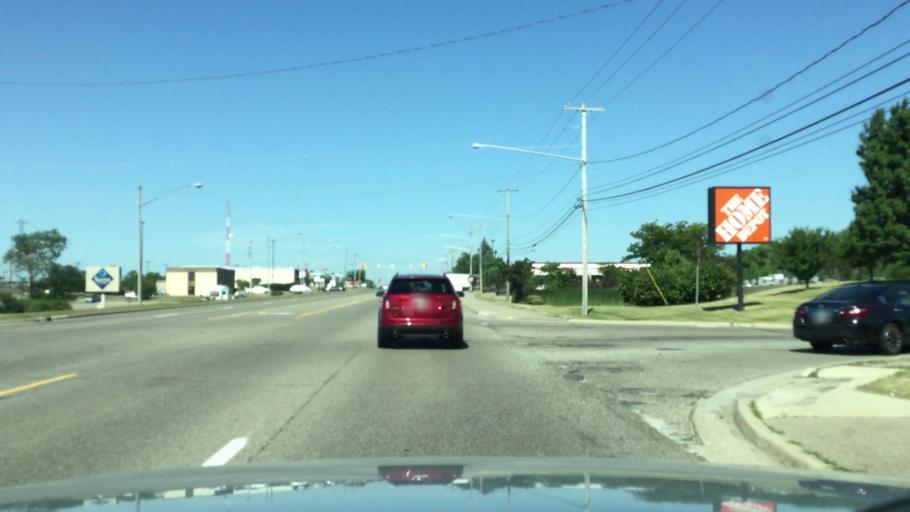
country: US
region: Michigan
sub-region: Genesee County
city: Flint
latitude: 43.0021
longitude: -83.7653
